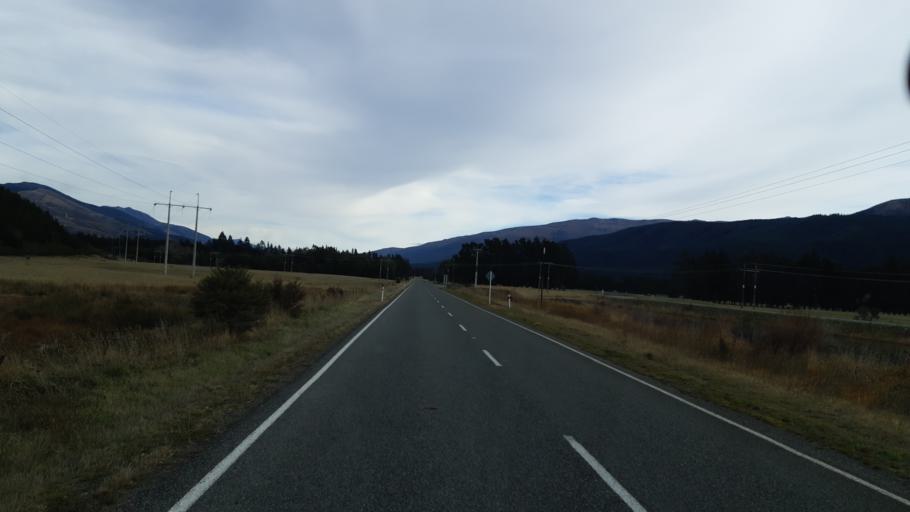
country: NZ
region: Tasman
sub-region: Tasman District
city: Brightwater
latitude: -41.6635
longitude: 173.2100
